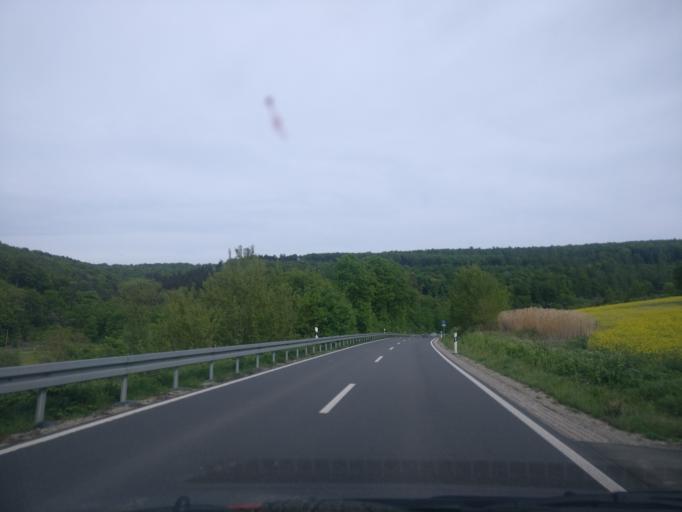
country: DE
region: Hesse
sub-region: Regierungsbezirk Kassel
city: Fuldatal
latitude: 51.3729
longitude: 9.5712
